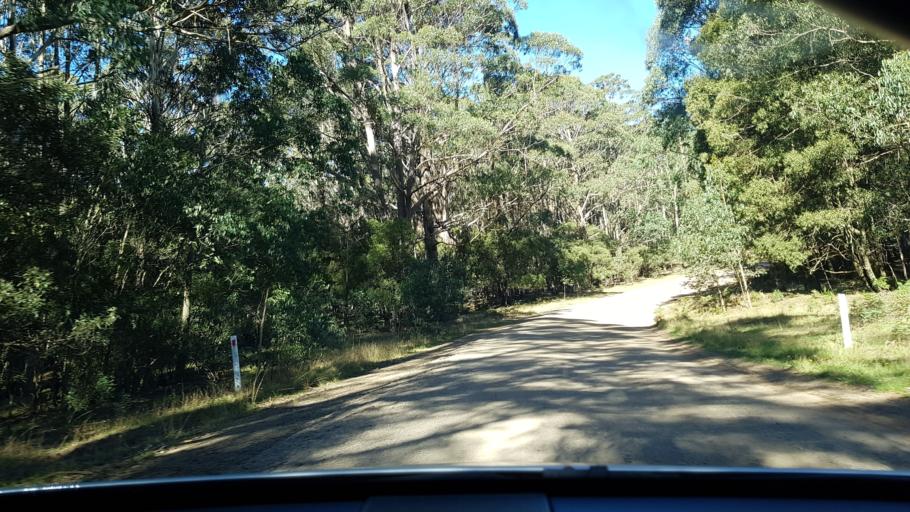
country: AU
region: New South Wales
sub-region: Oberon
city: Oberon
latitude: -33.8343
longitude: 150.0119
